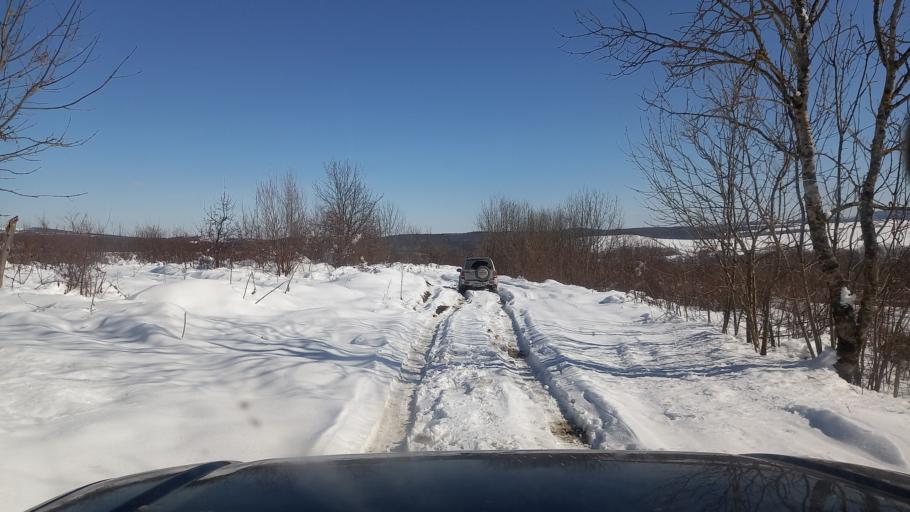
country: RU
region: Krasnodarskiy
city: Gubskaya
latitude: 44.3394
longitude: 40.4407
